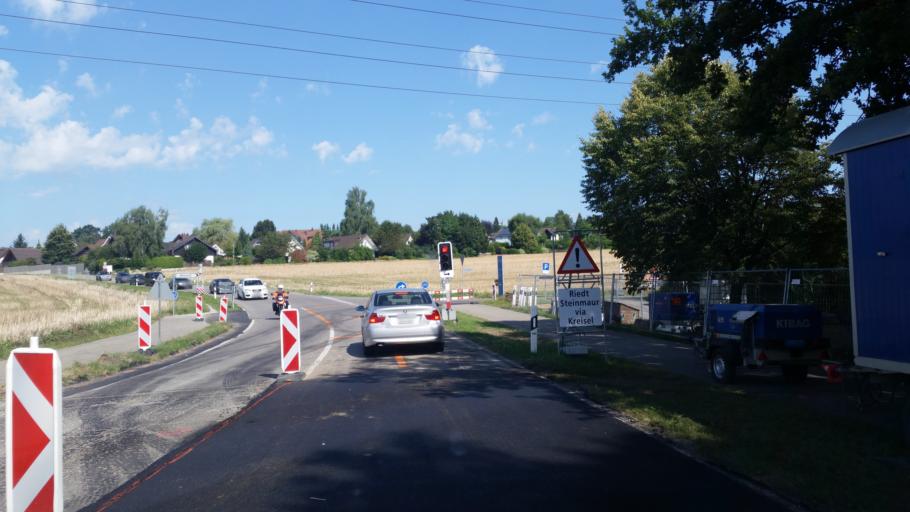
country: CH
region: Zurich
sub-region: Bezirk Dielsdorf
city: Neerach
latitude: 47.4998
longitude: 8.4777
